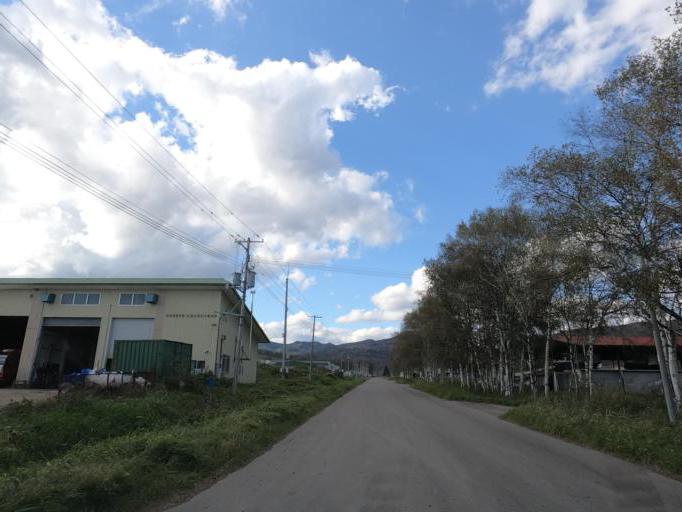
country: JP
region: Hokkaido
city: Otofuke
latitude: 43.2844
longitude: 143.2365
